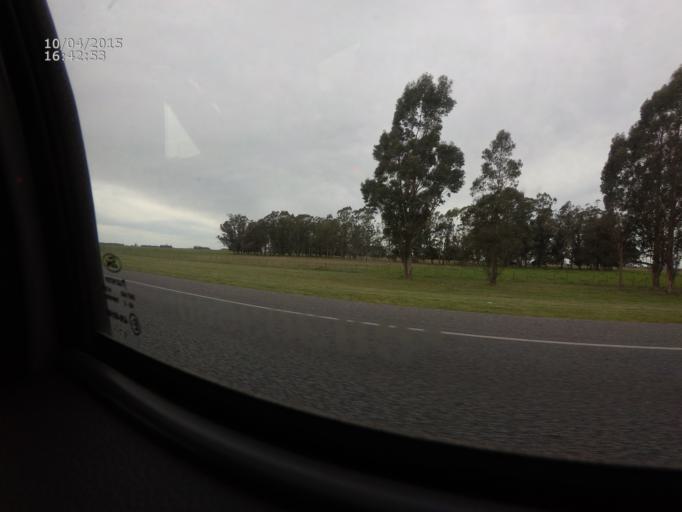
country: AR
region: Buenos Aires
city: Mar del Plata
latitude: -37.7529
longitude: -57.6429
